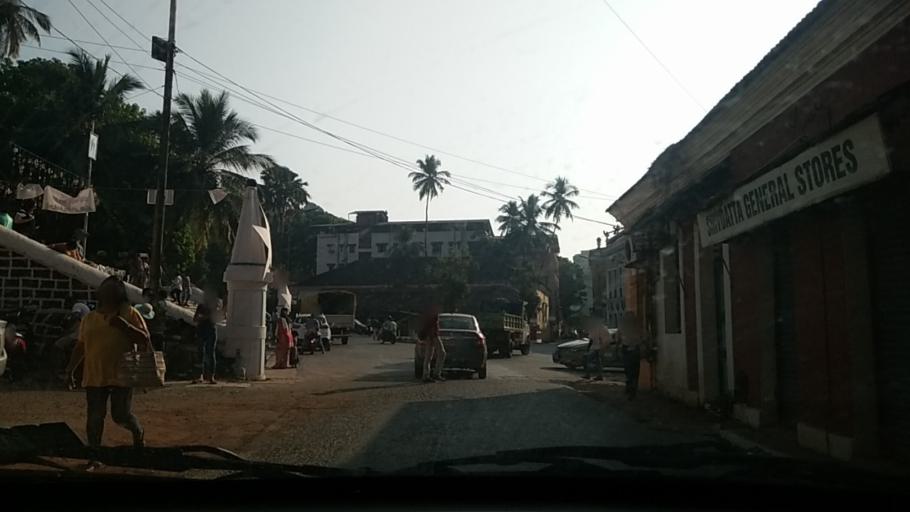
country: IN
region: Goa
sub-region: North Goa
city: Panaji
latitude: 15.4989
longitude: 73.8290
